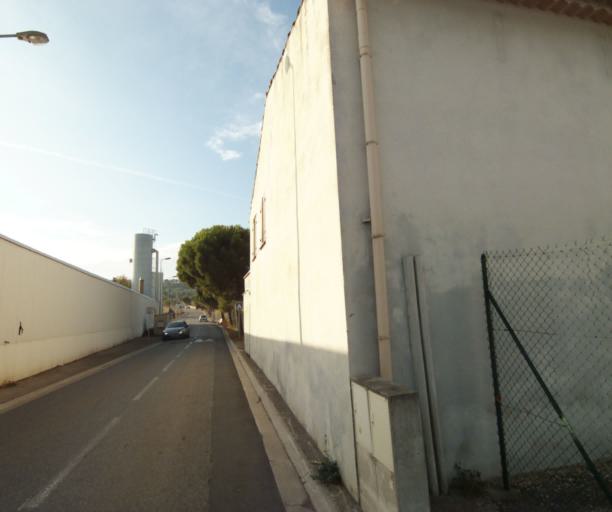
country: FR
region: Provence-Alpes-Cote d'Azur
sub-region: Departement des Bouches-du-Rhone
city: Saint-Victoret
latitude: 43.4153
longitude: 5.2654
